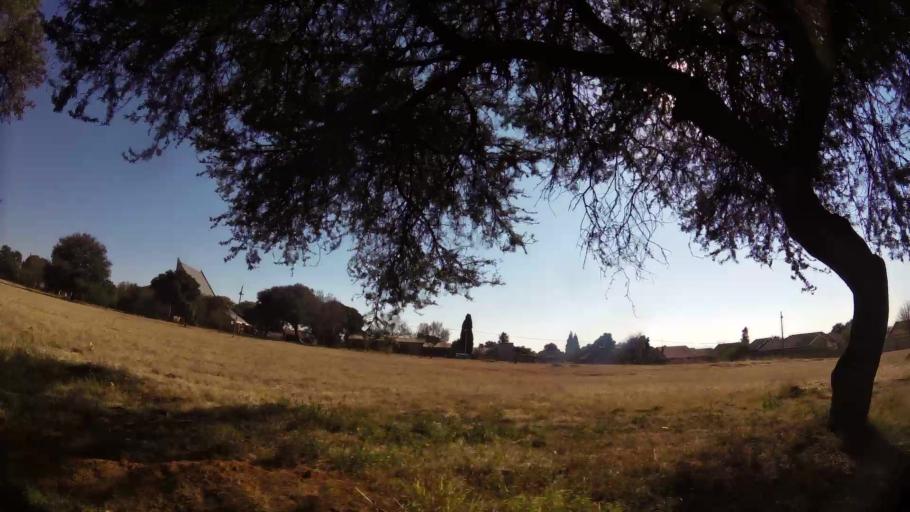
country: ZA
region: Gauteng
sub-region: Ekurhuleni Metropolitan Municipality
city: Germiston
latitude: -26.2556
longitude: 28.1038
